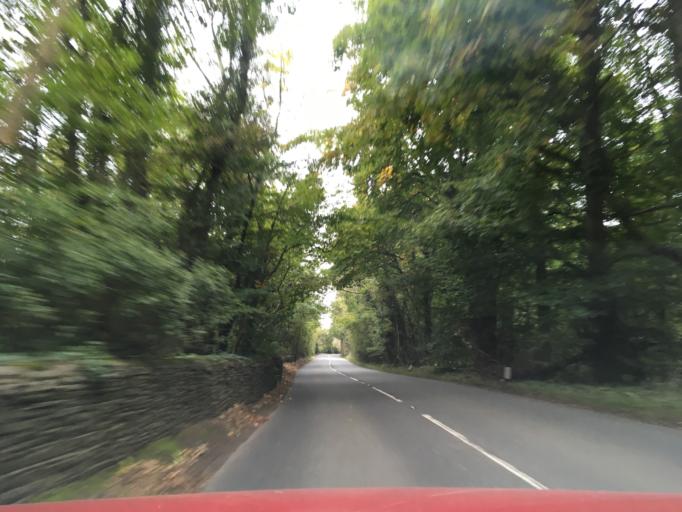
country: GB
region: England
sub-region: Gloucestershire
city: Dursley
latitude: 51.6696
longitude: -2.3174
